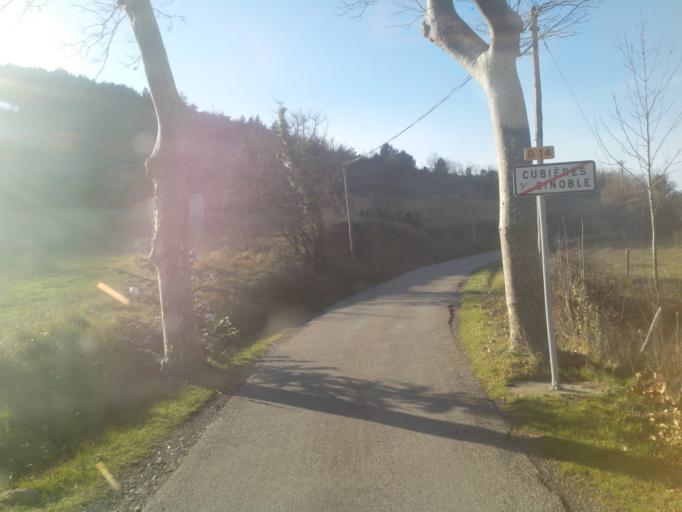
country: FR
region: Languedoc-Roussillon
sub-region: Departement des Pyrenees-Orientales
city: Saint-Paul-de-Fenouillet
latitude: 42.8618
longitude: 2.4591
